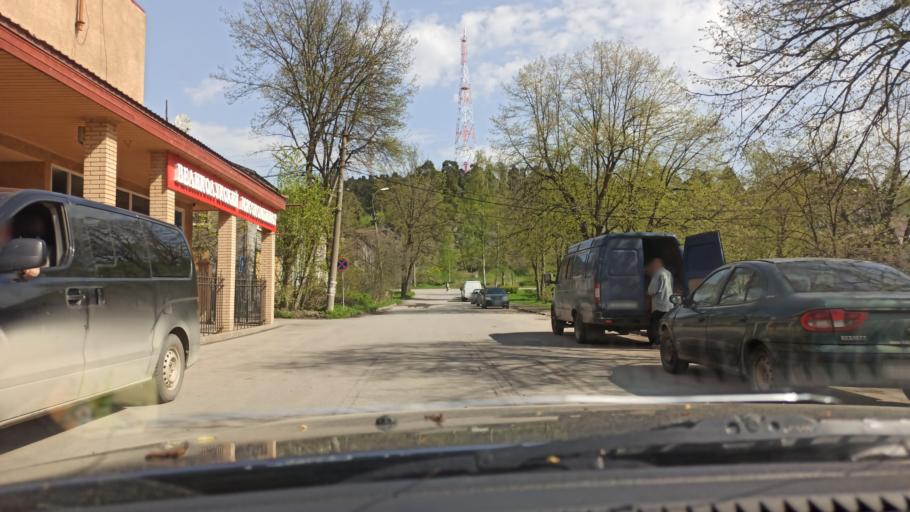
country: RU
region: Republic of Karelia
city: Lakhdenpokh'ya
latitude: 61.5202
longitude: 30.1980
